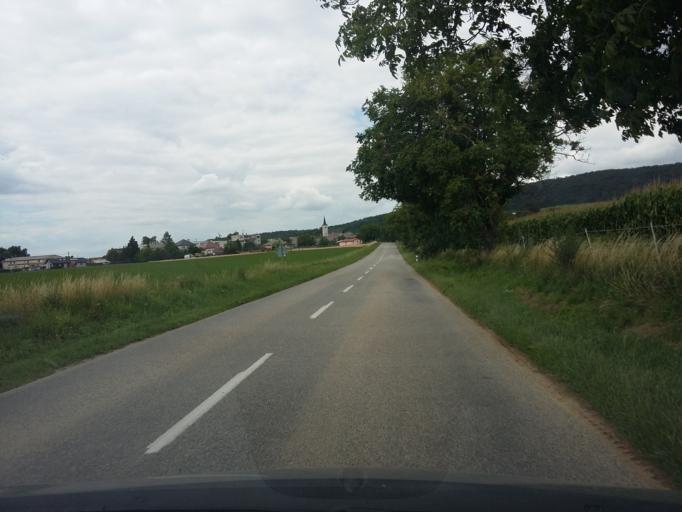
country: SK
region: Trnavsky
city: Smolenice
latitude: 48.5491
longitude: 17.3491
